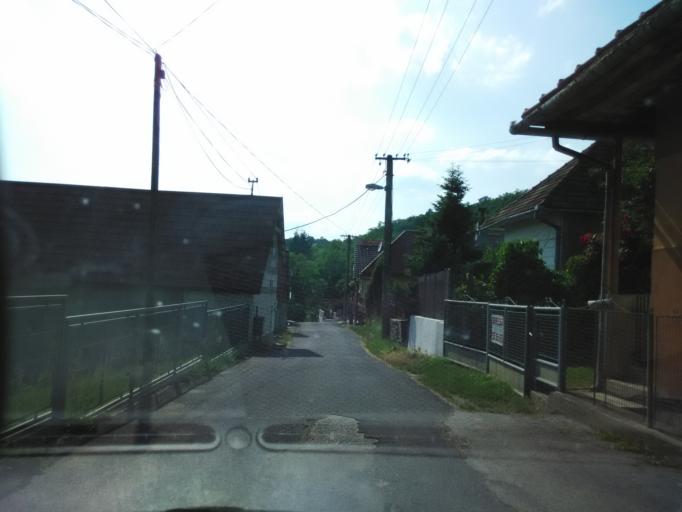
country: SK
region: Nitriansky
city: Levice
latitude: 48.2401
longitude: 18.6963
